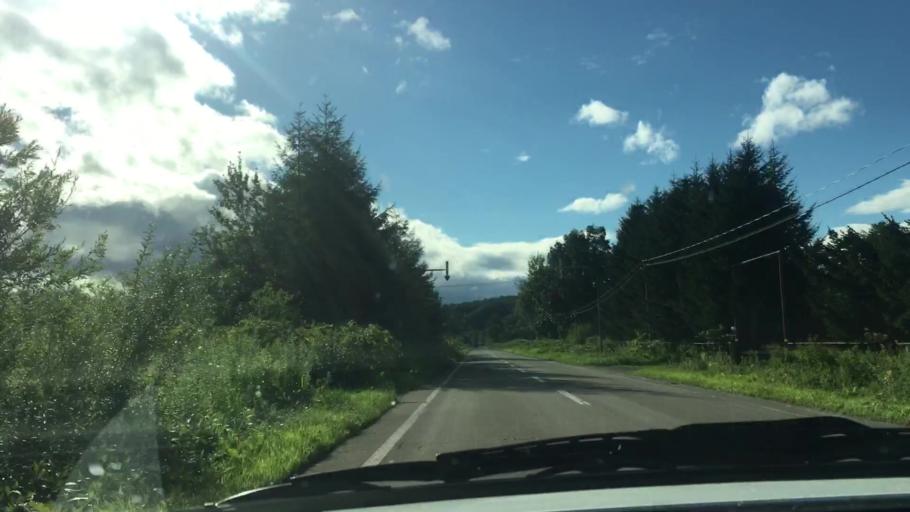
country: JP
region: Hokkaido
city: Otofuke
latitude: 43.1703
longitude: 142.9995
